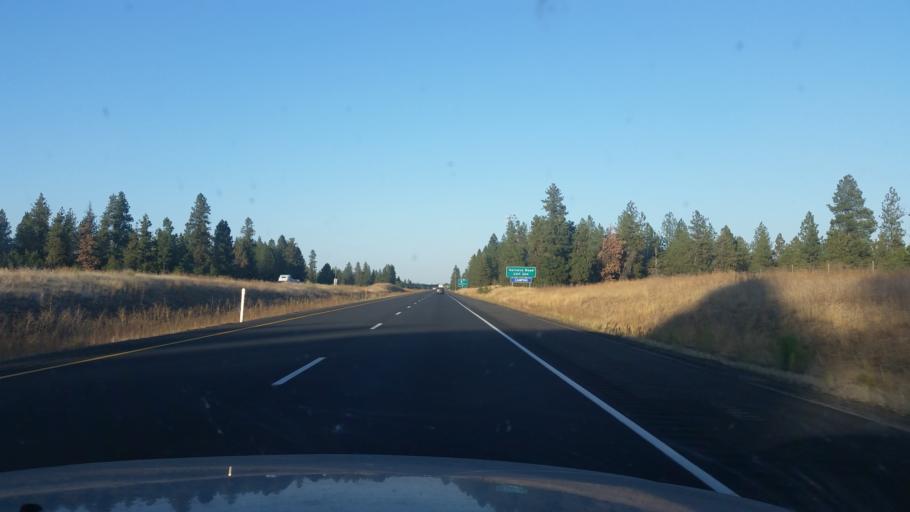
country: US
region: Washington
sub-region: Spokane County
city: Medical Lake
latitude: 47.4984
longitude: -117.6990
